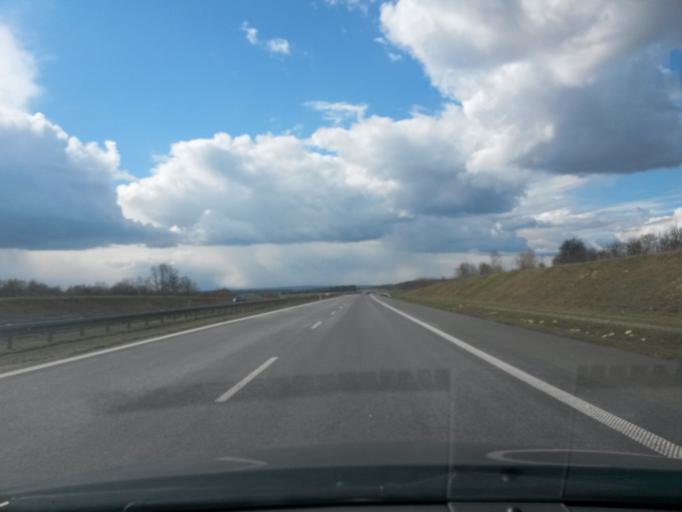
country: PL
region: Greater Poland Voivodeship
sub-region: Powiat turecki
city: Wladyslawow
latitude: 52.1451
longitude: 18.5134
